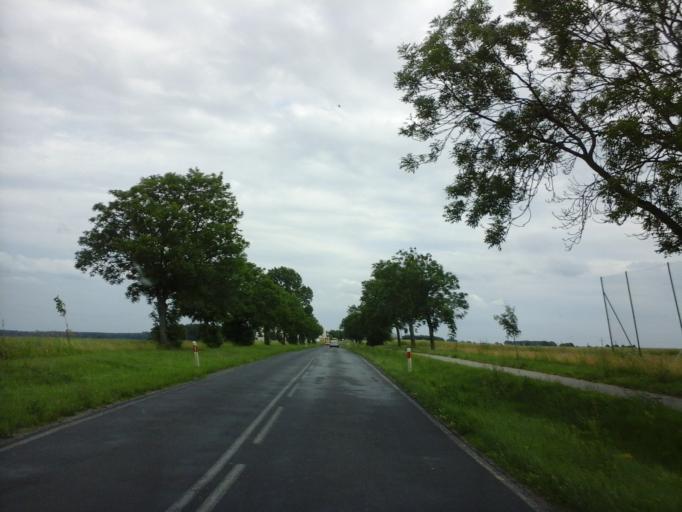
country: PL
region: West Pomeranian Voivodeship
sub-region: Powiat stargardzki
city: Stargard Szczecinski
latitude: 53.2908
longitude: 15.0640
